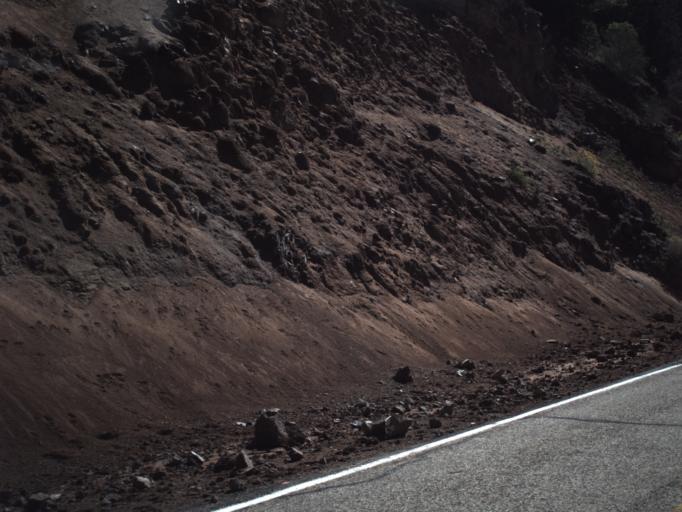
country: US
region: Utah
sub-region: Beaver County
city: Beaver
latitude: 38.2689
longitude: -112.4802
